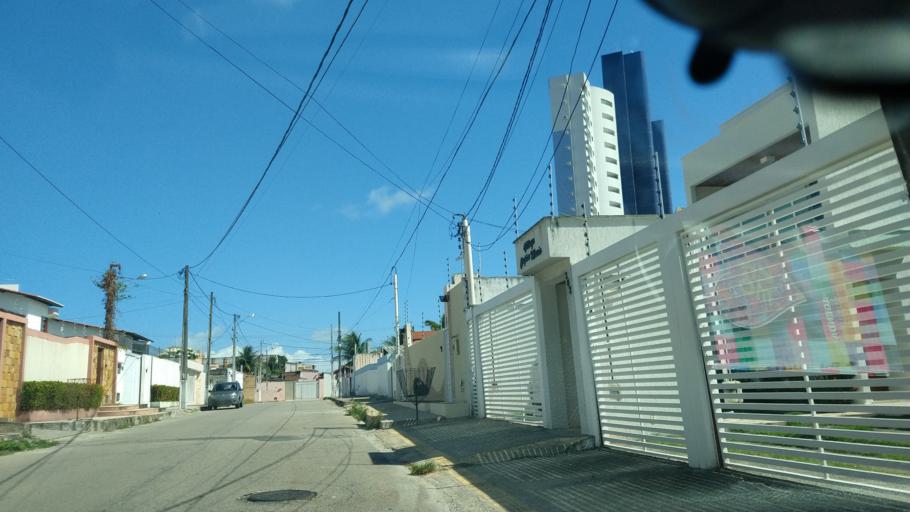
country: BR
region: Rio Grande do Norte
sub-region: Natal
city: Natal
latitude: -5.8710
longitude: -35.1909
